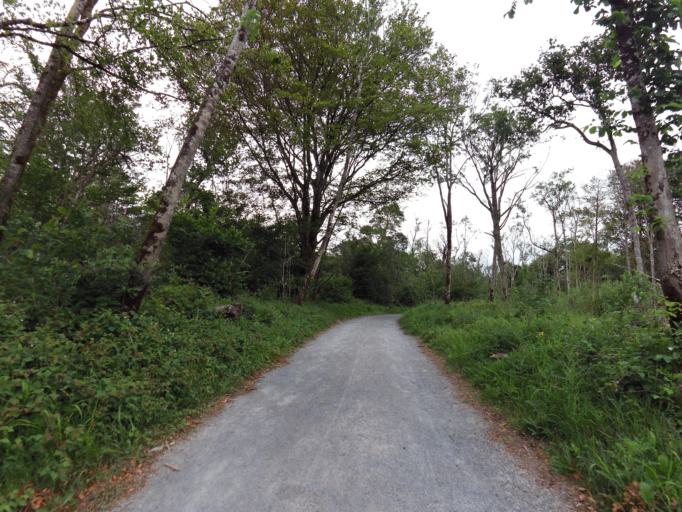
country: IE
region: Connaught
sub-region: County Galway
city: Gort
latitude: 53.0785
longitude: -8.8493
